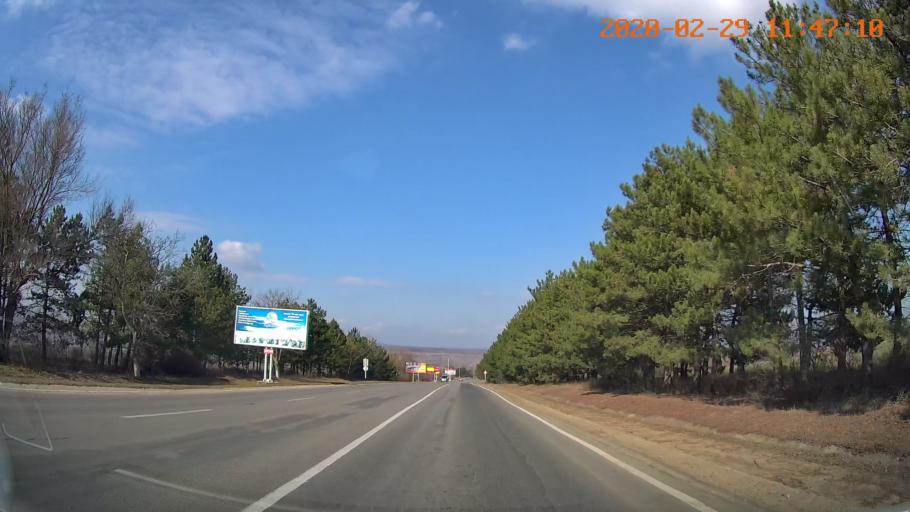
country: MD
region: Rezina
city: Rezina
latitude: 47.7383
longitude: 28.9897
